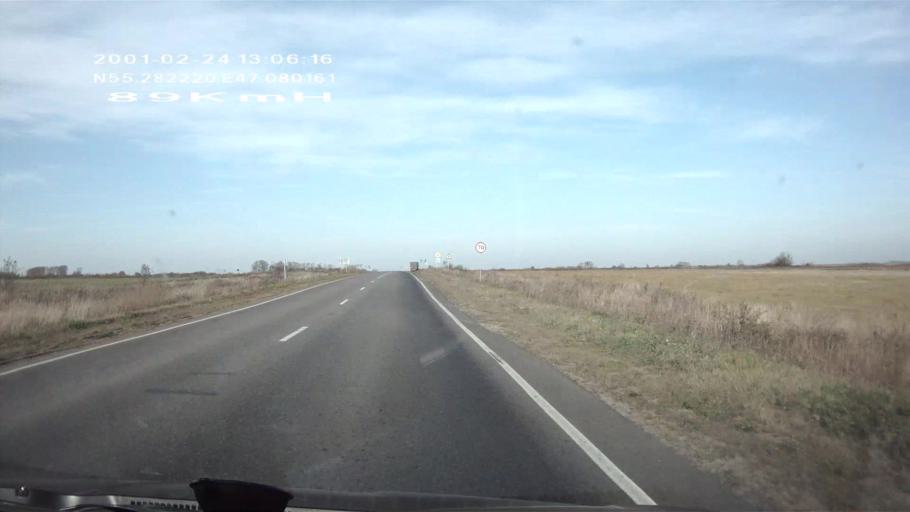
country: RU
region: Chuvashia
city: Ibresi
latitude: 55.2821
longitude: 47.0802
